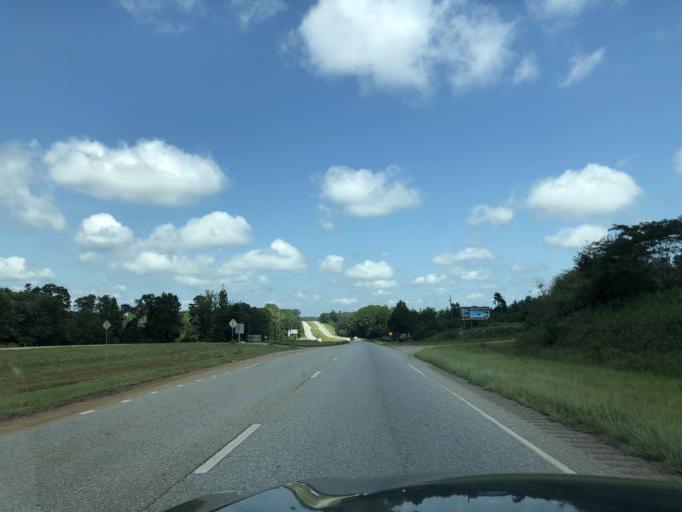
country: US
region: Alabama
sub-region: Henry County
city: Abbeville
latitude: 31.6226
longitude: -85.2778
